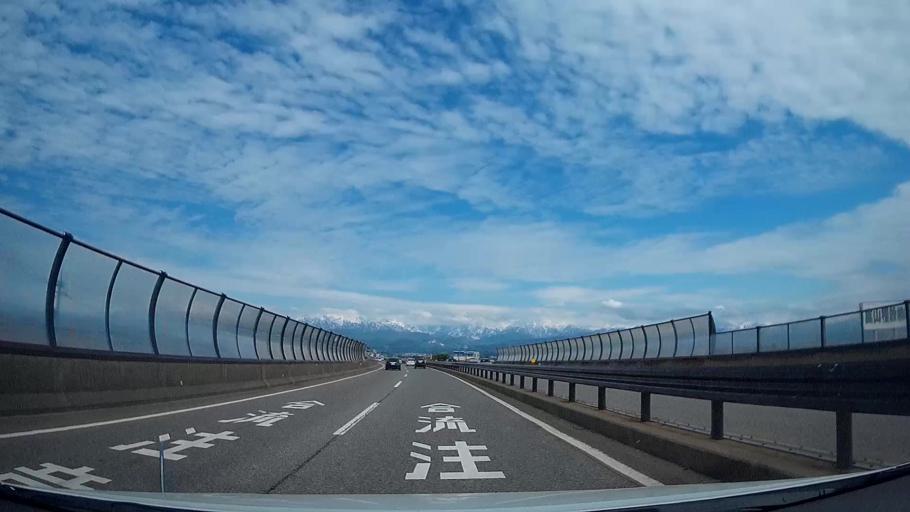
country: JP
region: Toyama
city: Toyama-shi
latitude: 36.7194
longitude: 137.2667
